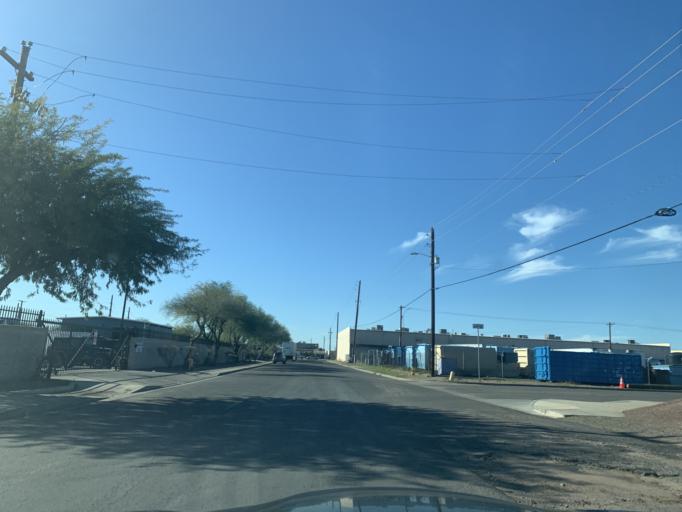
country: US
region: Arizona
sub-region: Maricopa County
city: Tempe Junction
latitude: 33.4183
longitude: -111.9848
